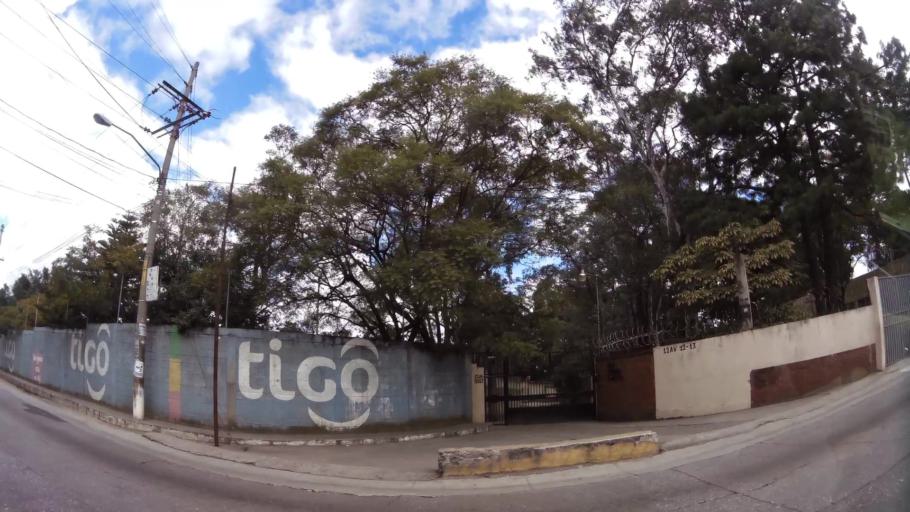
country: GT
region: Guatemala
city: Mixco
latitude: 14.6391
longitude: -90.5996
